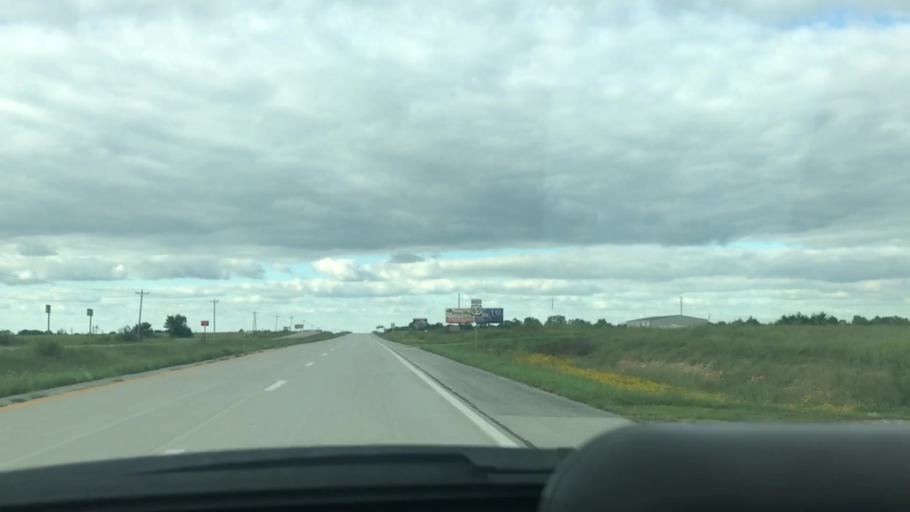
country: US
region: Missouri
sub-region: Benton County
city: Lincoln
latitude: 38.3410
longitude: -93.3405
